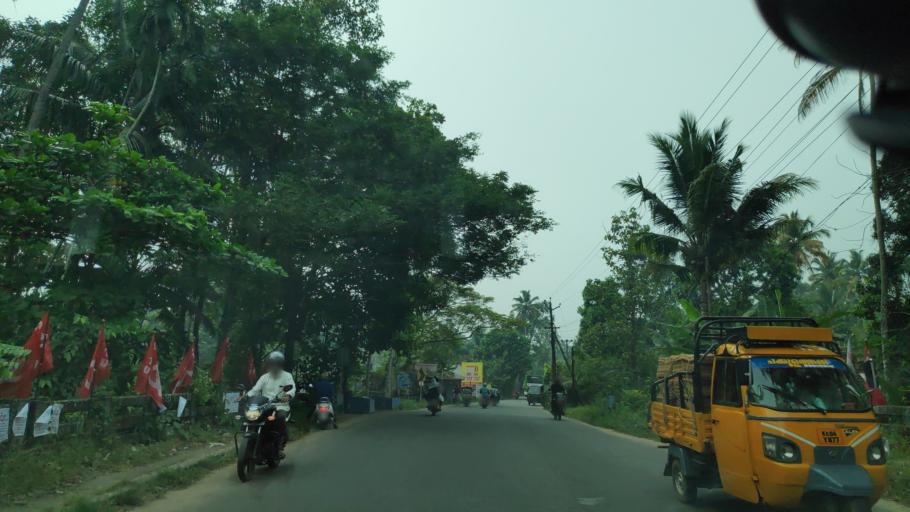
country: IN
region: Kerala
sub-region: Alappuzha
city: Alleppey
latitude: 9.5699
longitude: 76.3478
